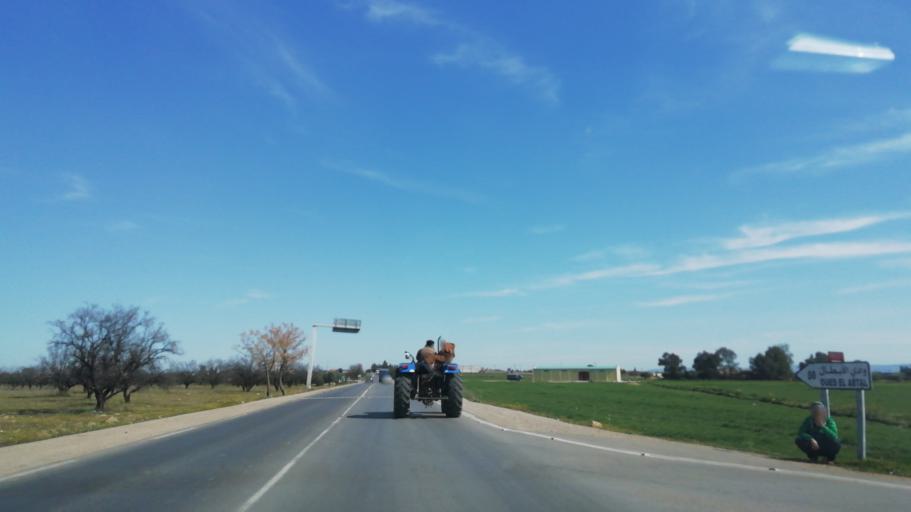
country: DZ
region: Mascara
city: Mascara
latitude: 35.4147
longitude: 0.3744
